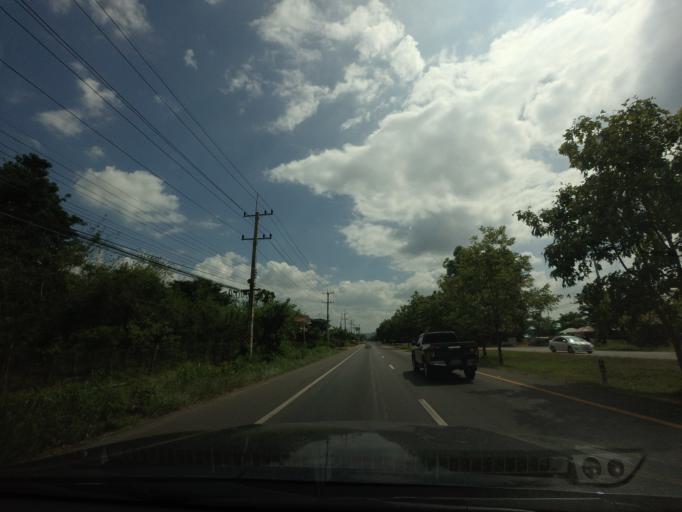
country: TH
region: Phetchabun
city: Wichian Buri
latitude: 15.7360
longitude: 101.0143
